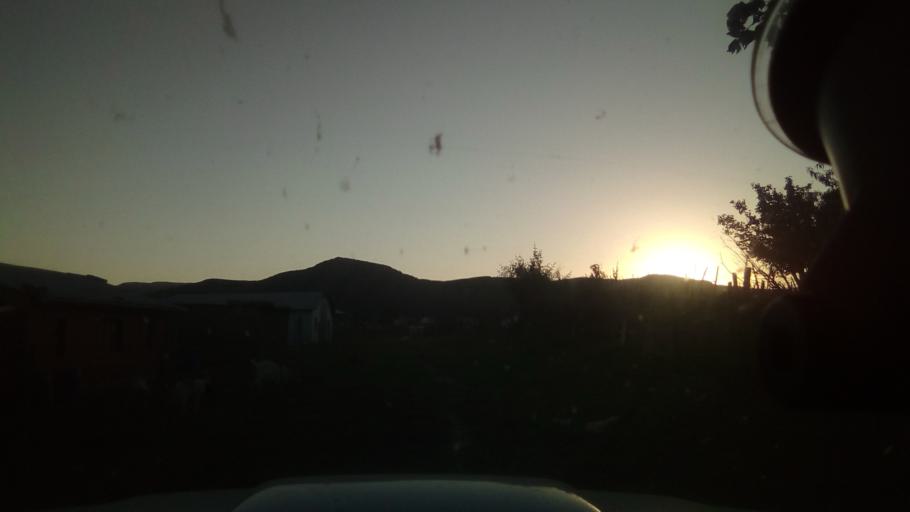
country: ZA
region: Eastern Cape
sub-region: Buffalo City Metropolitan Municipality
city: Bhisho
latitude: -32.7353
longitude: 27.3749
